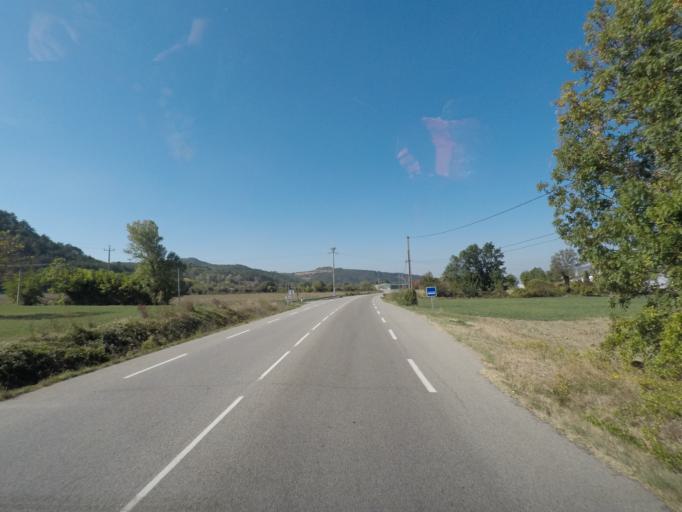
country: FR
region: Rhone-Alpes
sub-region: Departement de la Drome
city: Aouste-sur-Sye
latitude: 44.7090
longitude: 5.0696
